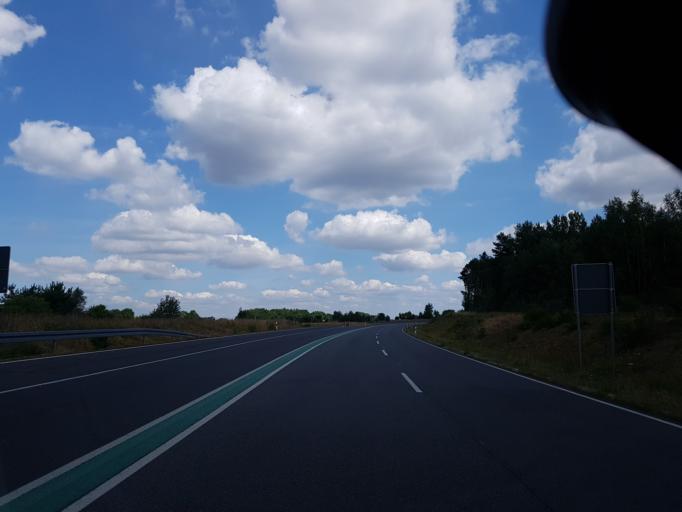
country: DE
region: Brandenburg
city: Drebkau
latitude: 51.6627
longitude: 14.2412
